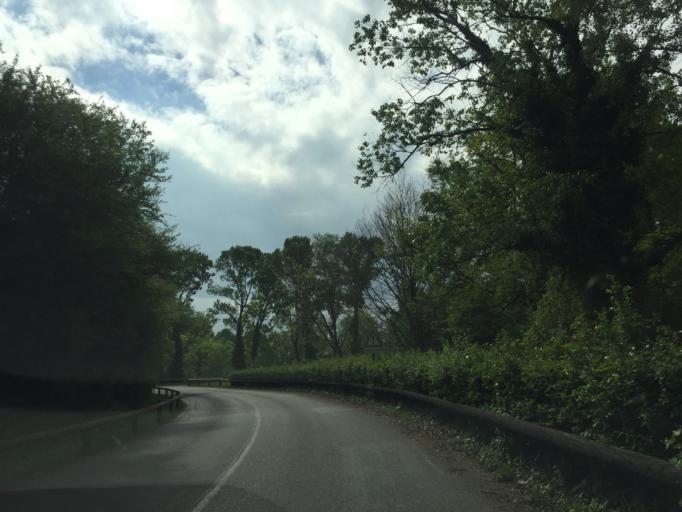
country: FR
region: Rhone-Alpes
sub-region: Departement du Rhone
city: Vaulx-en-Velin
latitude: 45.7984
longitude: 4.9379
